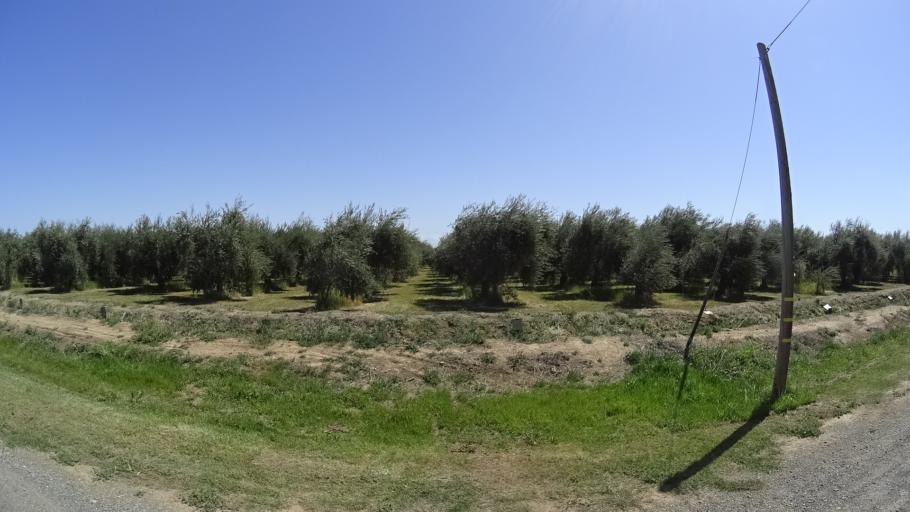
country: US
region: California
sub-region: Glenn County
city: Orland
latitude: 39.7738
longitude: -122.1830
